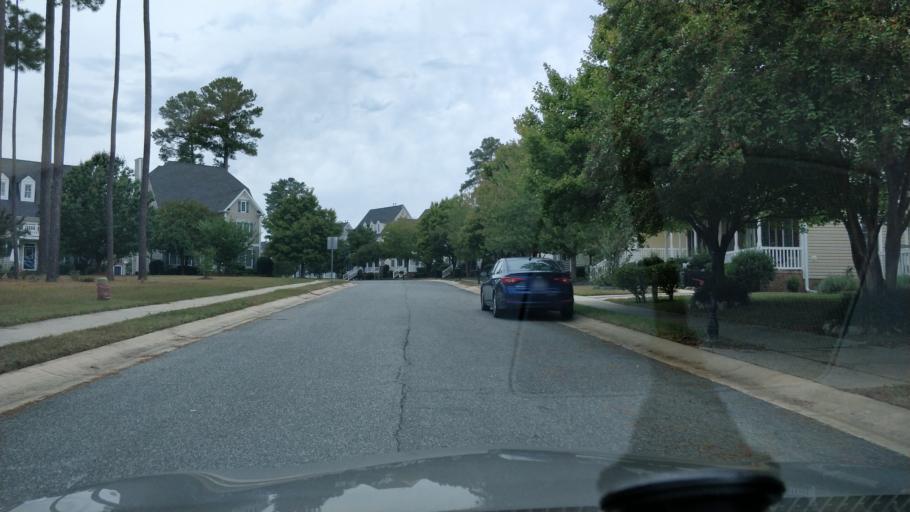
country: US
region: North Carolina
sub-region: Wake County
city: Morrisville
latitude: 35.8215
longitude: -78.8334
